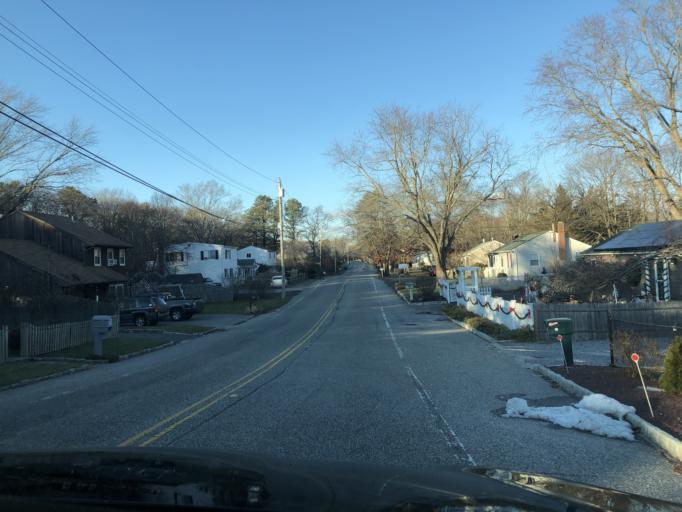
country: US
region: New York
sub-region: Suffolk County
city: Wading River
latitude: 40.9102
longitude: -72.8465
